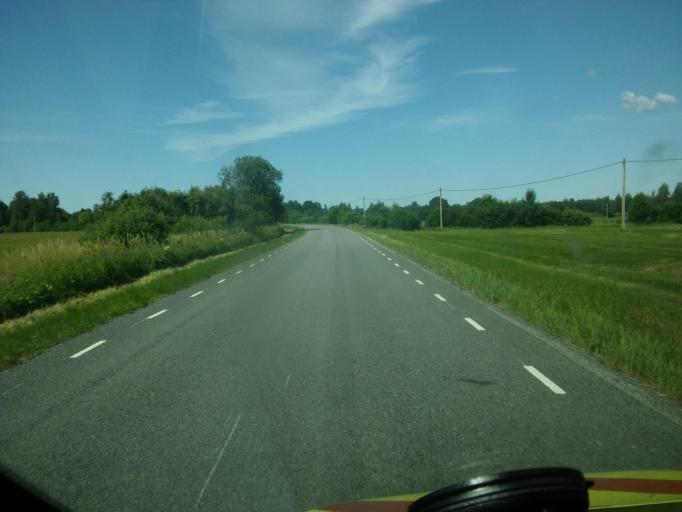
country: EE
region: Paernumaa
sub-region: Paikuse vald
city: Paikuse
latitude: 58.2461
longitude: 24.7343
